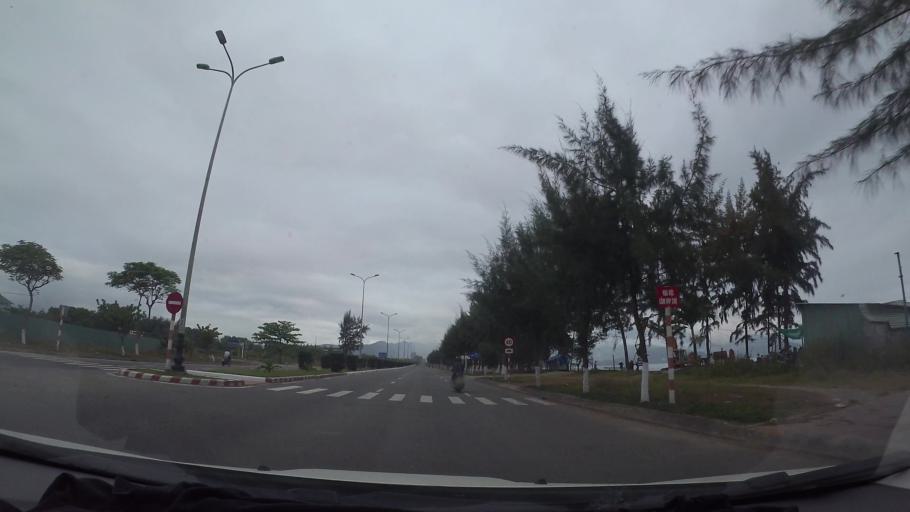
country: VN
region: Da Nang
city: Lien Chieu
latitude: 16.0958
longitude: 108.1454
